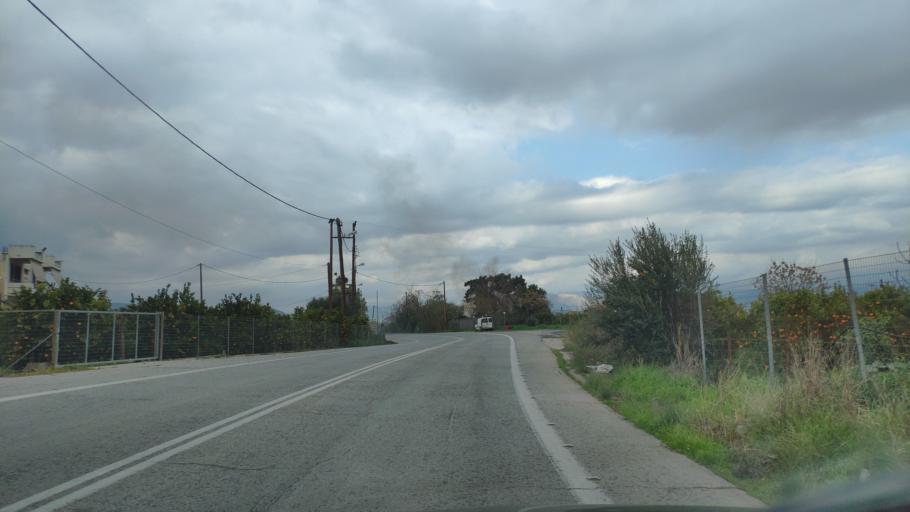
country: GR
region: Peloponnese
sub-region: Nomos Argolidos
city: Nea Kios
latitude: 37.5776
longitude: 22.7088
